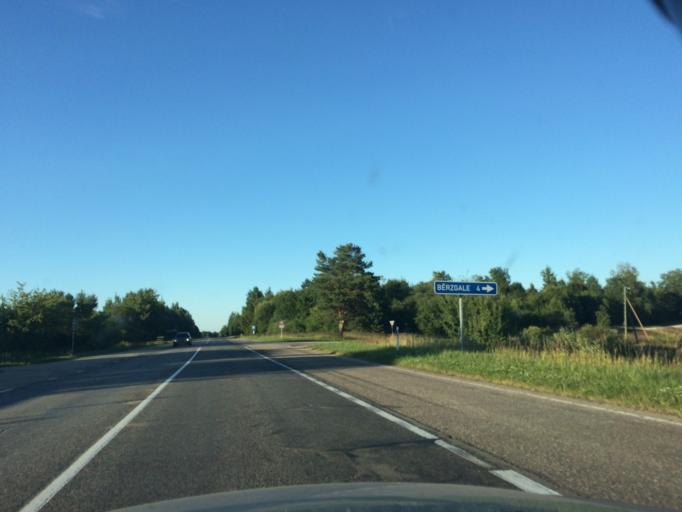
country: LV
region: Rezekne
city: Rezekne
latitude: 56.6148
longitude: 27.4481
